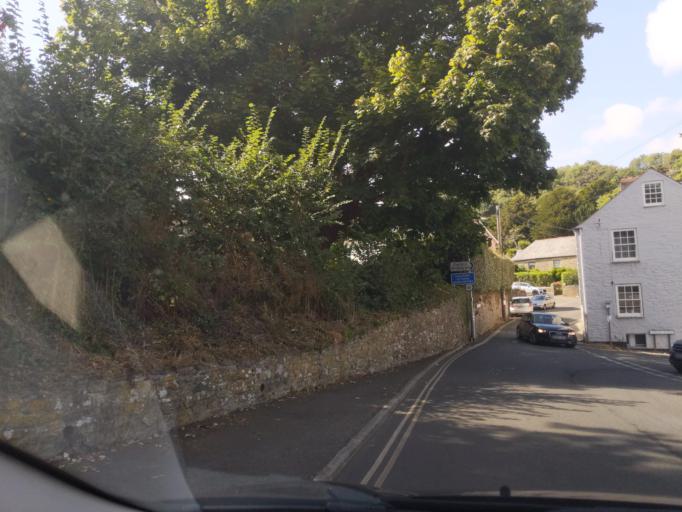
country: GB
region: England
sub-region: Devon
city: Salcombe
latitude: 50.2392
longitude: -3.7706
